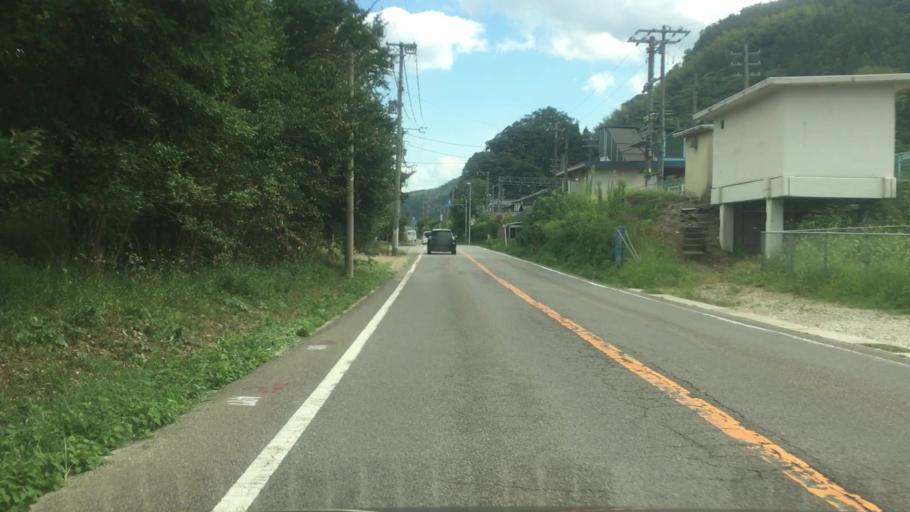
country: JP
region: Hyogo
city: Toyooka
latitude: 35.5892
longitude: 134.7993
